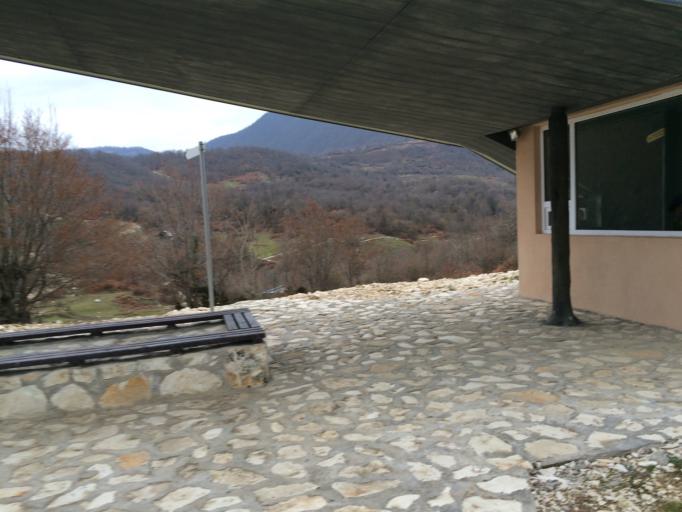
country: GE
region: Imereti
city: Tsqaltubo
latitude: 42.4547
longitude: 42.5495
